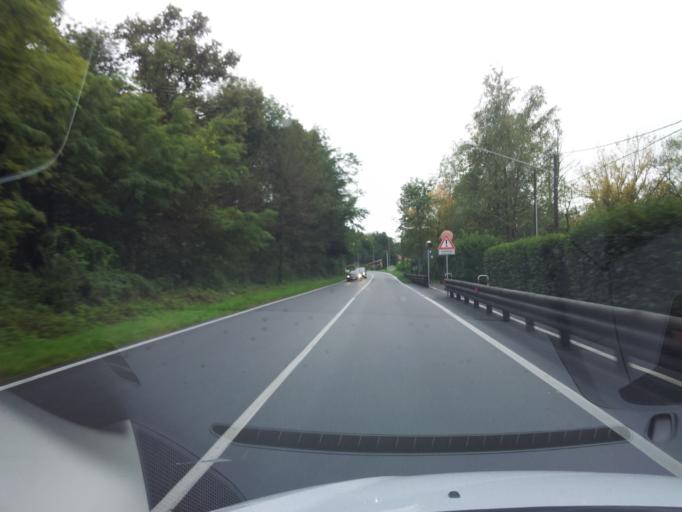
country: IT
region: Lombardy
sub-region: Provincia di Varese
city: Corgeno
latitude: 45.7556
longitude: 8.6985
